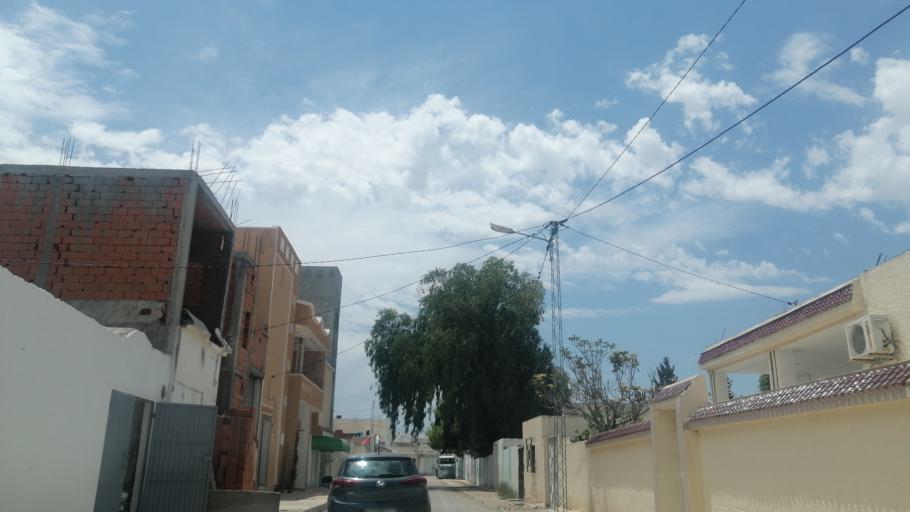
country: TN
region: Al Qayrawan
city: Sbikha
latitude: 36.1257
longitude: 10.0938
